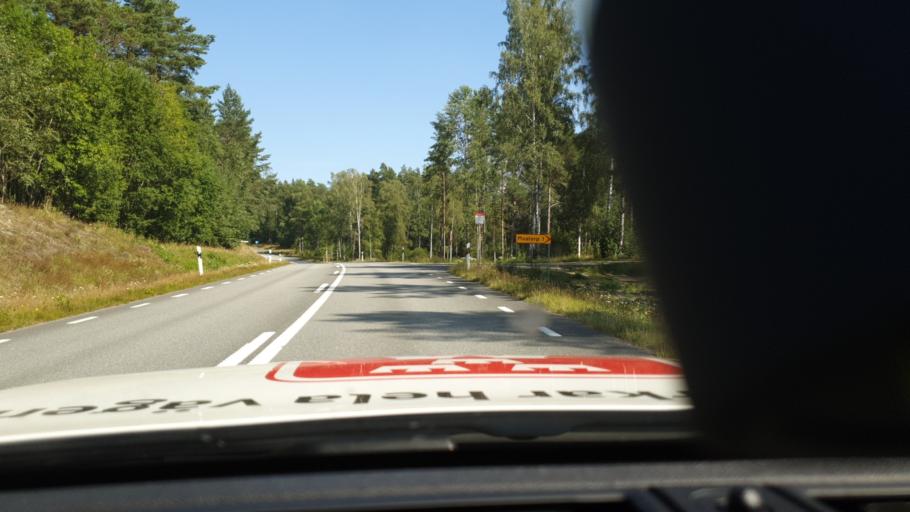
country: SE
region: Joenkoeping
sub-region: Nassjo Kommun
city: Bodafors
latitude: 57.4750
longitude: 14.7765
